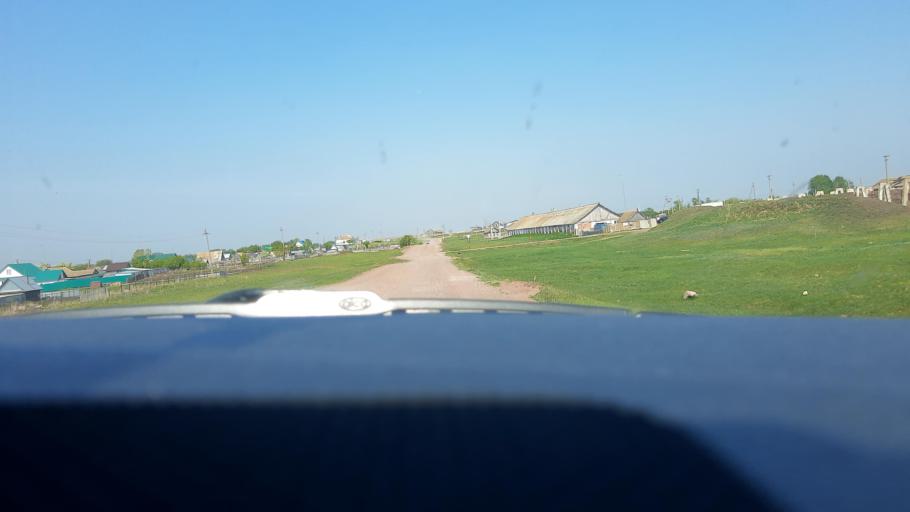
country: RU
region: Bashkortostan
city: Chishmy
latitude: 54.4429
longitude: 55.3134
